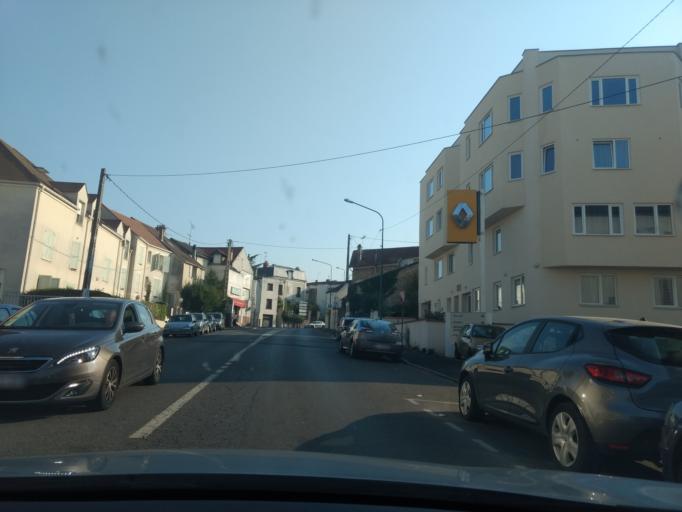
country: FR
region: Ile-de-France
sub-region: Departement de l'Essonne
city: Palaiseau
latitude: 48.7171
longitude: 2.2488
